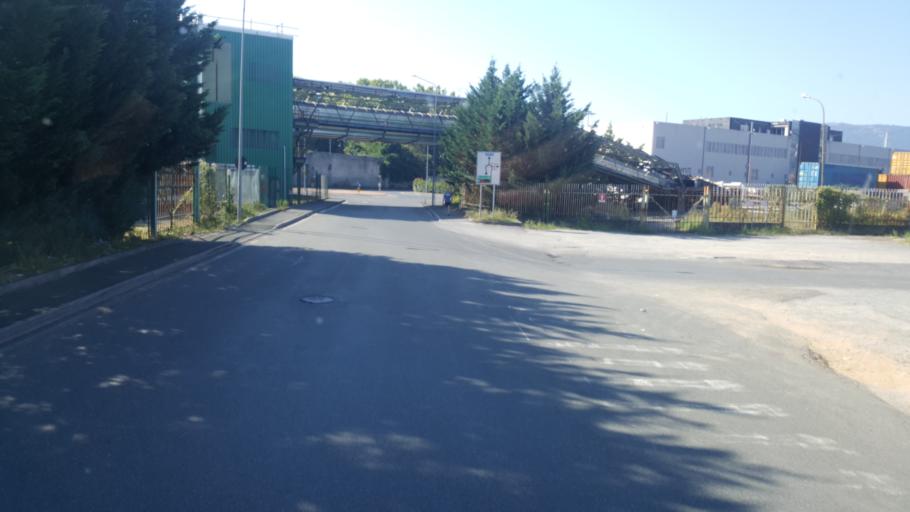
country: IT
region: Liguria
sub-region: Provincia di La Spezia
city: La Spezia
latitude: 44.1064
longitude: 9.8606
